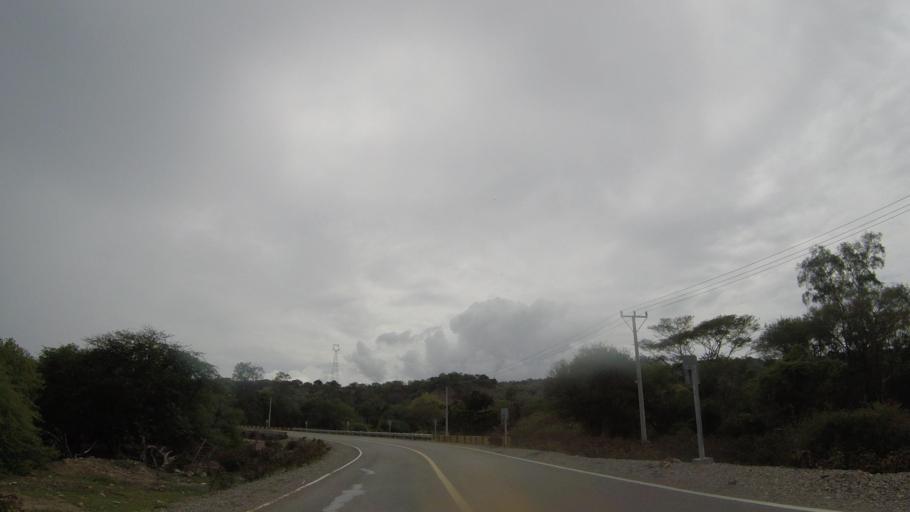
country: TL
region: Lautem
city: Lospalos
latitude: -8.4200
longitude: 126.7831
